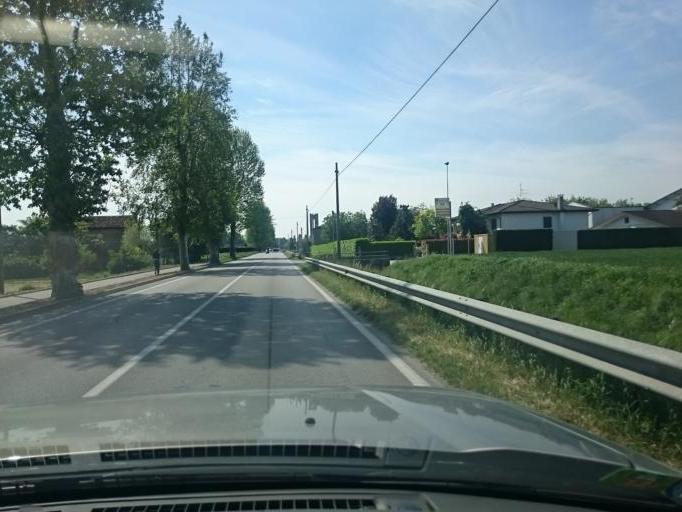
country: IT
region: Veneto
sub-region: Provincia di Padova
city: Masera di Padova
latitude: 45.2949
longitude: 11.8691
